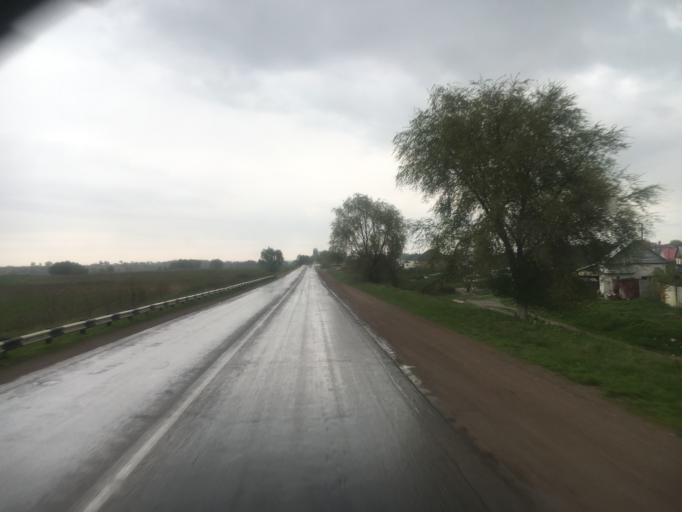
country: KZ
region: Almaty Oblysy
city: Burunday
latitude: 43.2915
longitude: 76.6733
